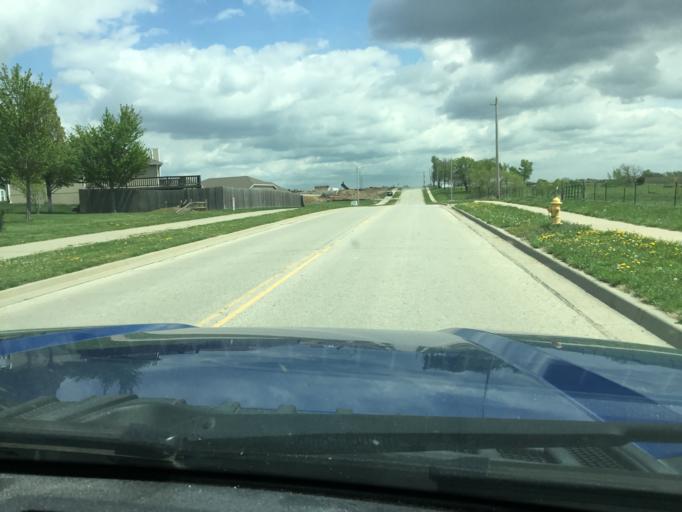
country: US
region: Kansas
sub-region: Douglas County
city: Eudora
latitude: 38.9132
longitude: -95.0977
